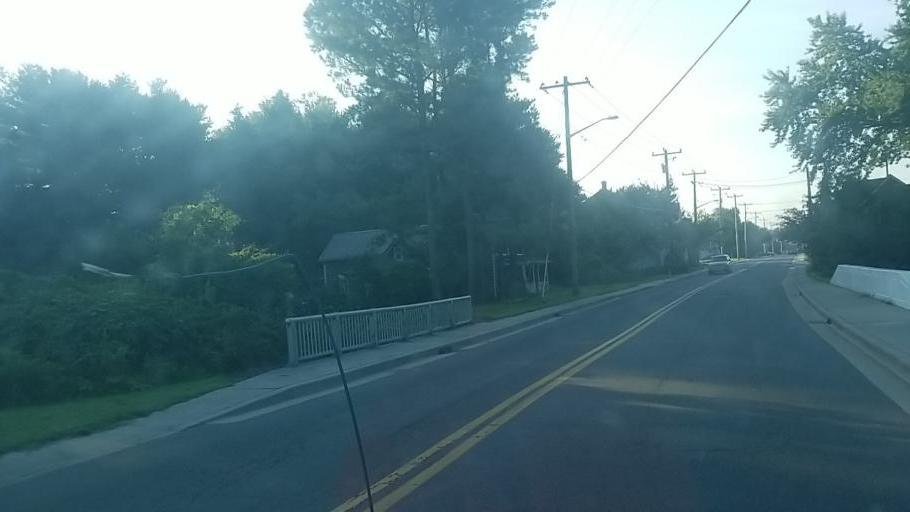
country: US
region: Delaware
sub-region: Sussex County
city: Selbyville
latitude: 38.4627
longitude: -75.2230
